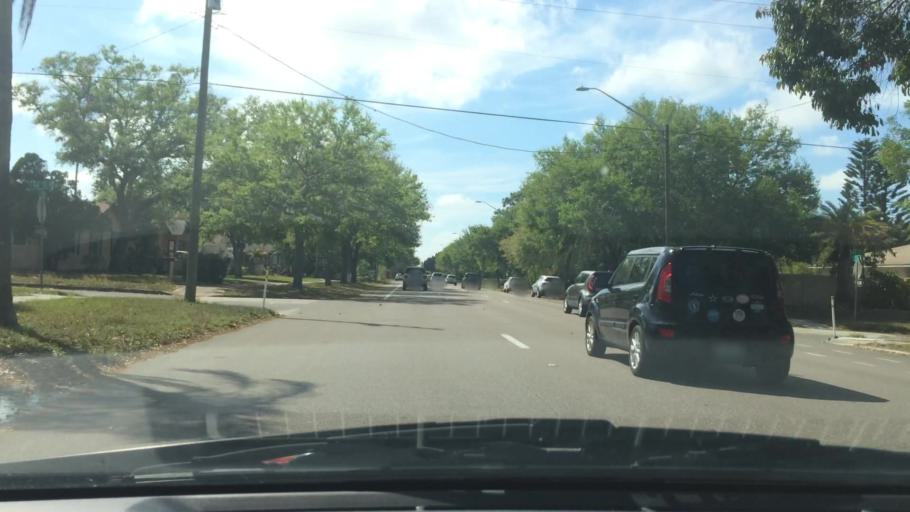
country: US
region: Florida
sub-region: Pinellas County
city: Saint Petersburg
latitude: 27.7718
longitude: -82.6928
